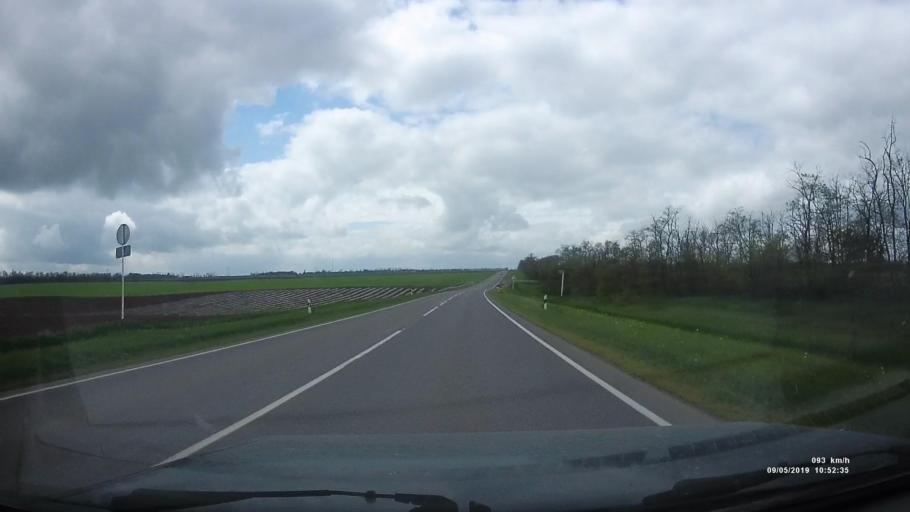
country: RU
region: Rostov
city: Peshkovo
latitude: 46.8989
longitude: 39.3517
